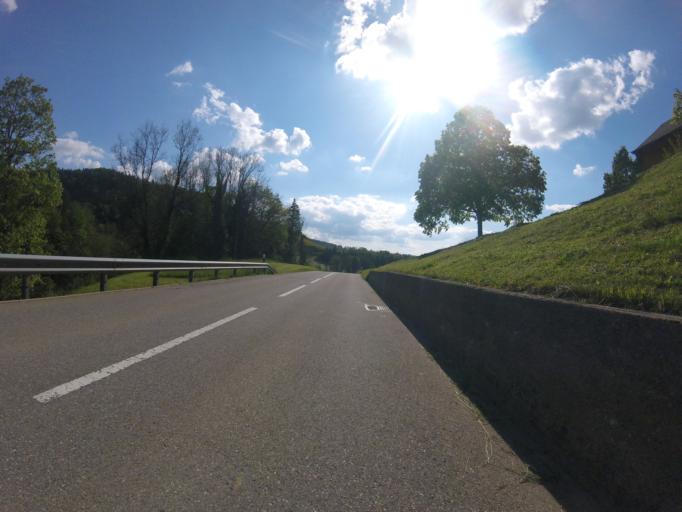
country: CH
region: Saint Gallen
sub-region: Wahlkreis Wil
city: Degersheim
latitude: 47.3617
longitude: 9.1791
